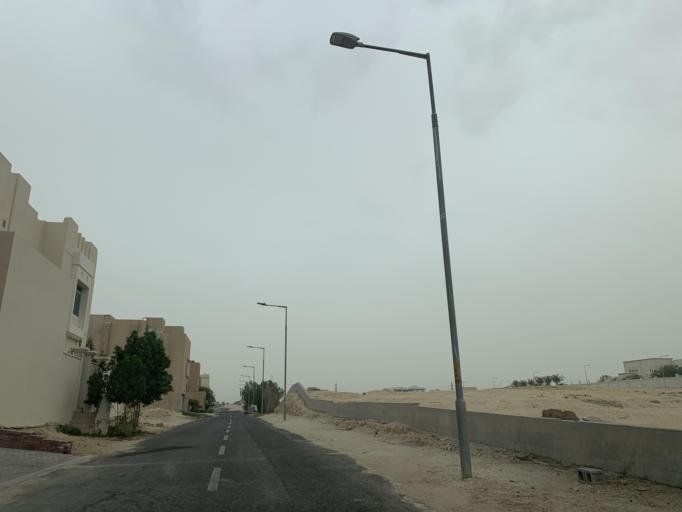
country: BH
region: Northern
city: Ar Rifa'
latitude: 26.1450
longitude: 50.5325
